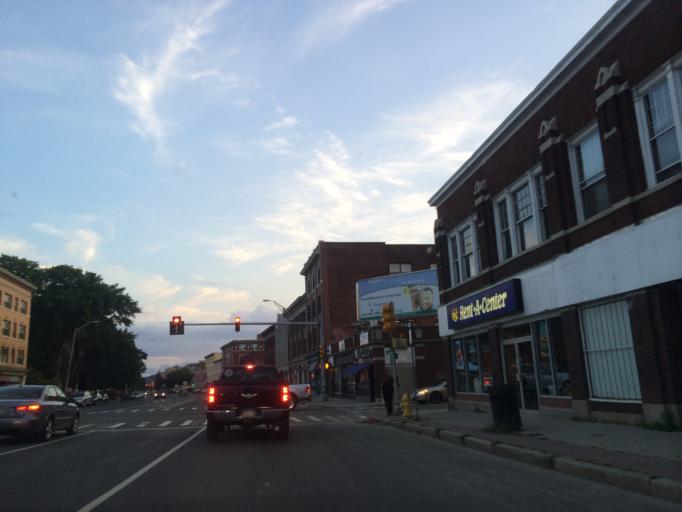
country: US
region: Massachusetts
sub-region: Berkshire County
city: Pittsfield
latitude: 42.4556
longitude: -73.2518
